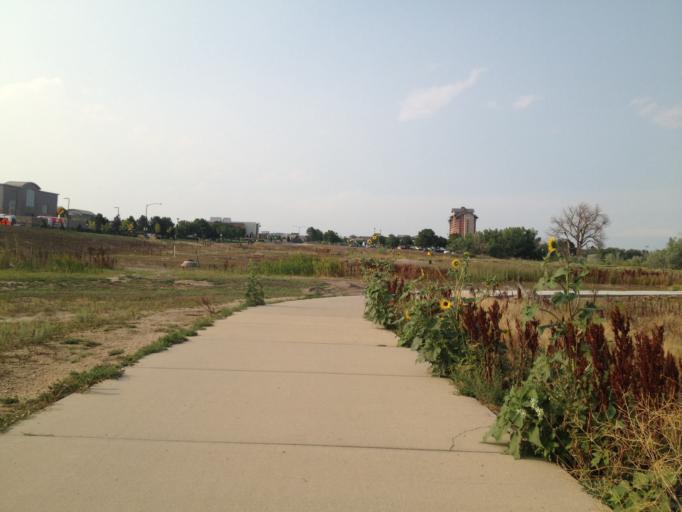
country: US
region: Colorado
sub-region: Broomfield County
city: Broomfield
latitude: 39.8837
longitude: -105.0673
